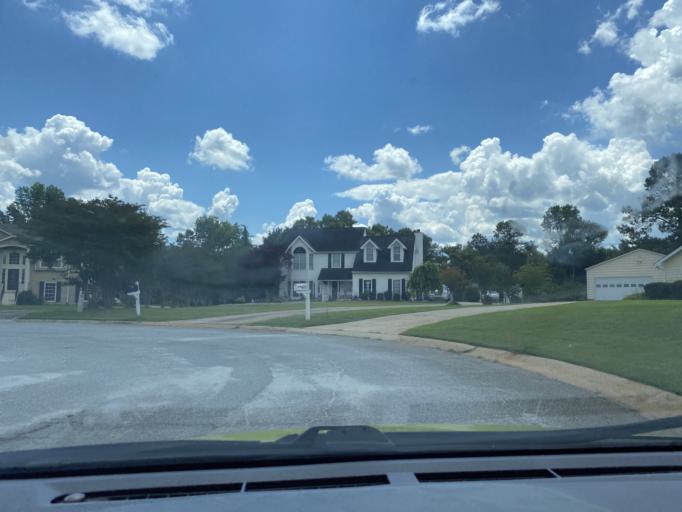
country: US
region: Georgia
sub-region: Fayette County
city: Peachtree City
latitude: 33.4113
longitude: -84.6740
